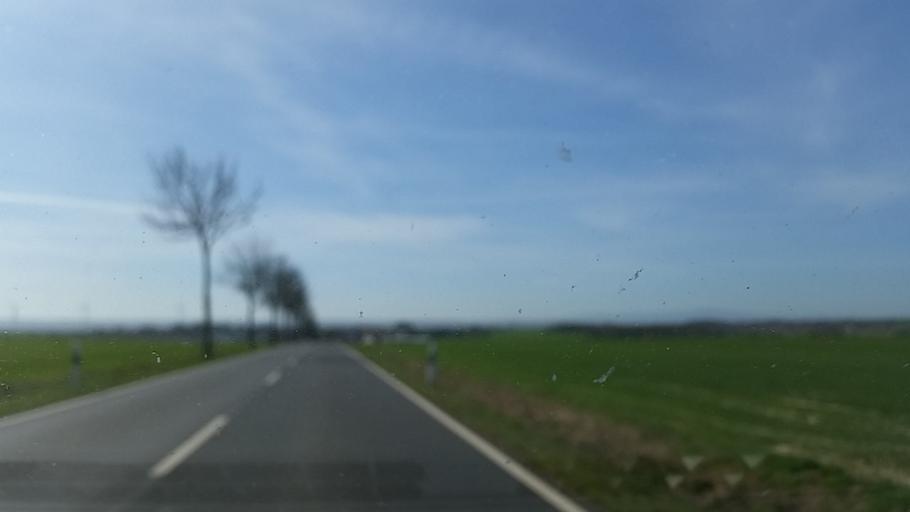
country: DE
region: Lower Saxony
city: Sollingen
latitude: 52.1067
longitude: 10.9273
